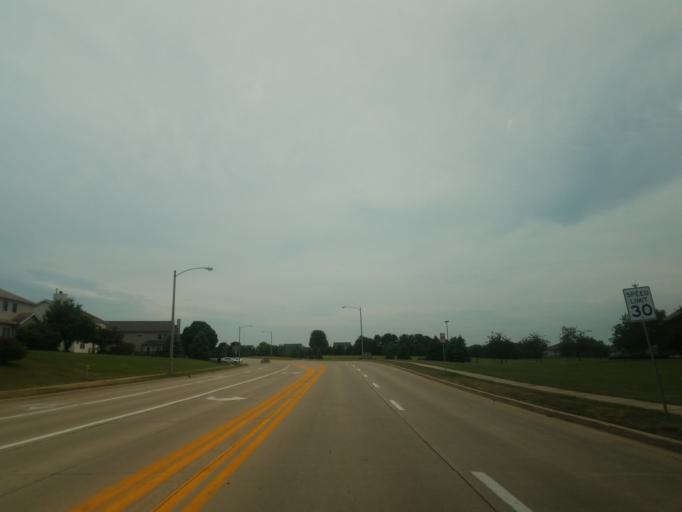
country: US
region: Illinois
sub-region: McLean County
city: Normal
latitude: 40.5175
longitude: -88.9437
